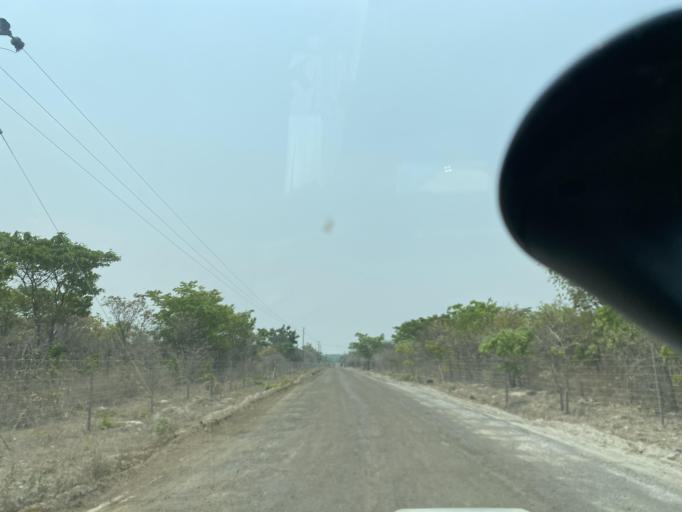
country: ZM
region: Lusaka
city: Lusaka
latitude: -15.5188
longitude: 28.4440
